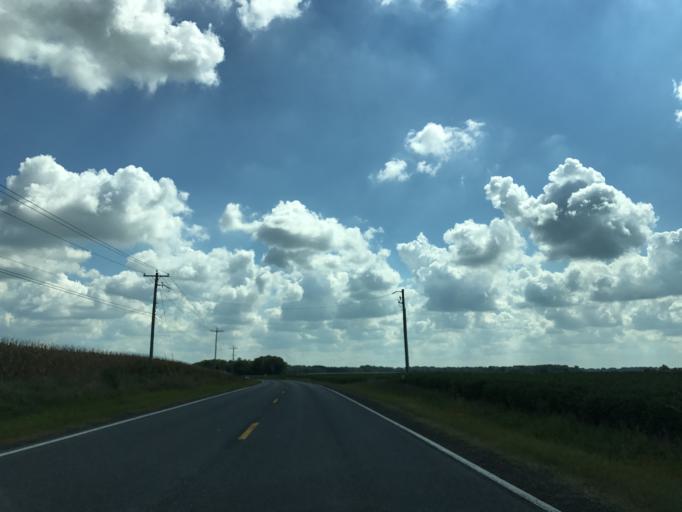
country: US
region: Maryland
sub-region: Queen Anne's County
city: Centreville
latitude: 39.0109
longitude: -75.9926
